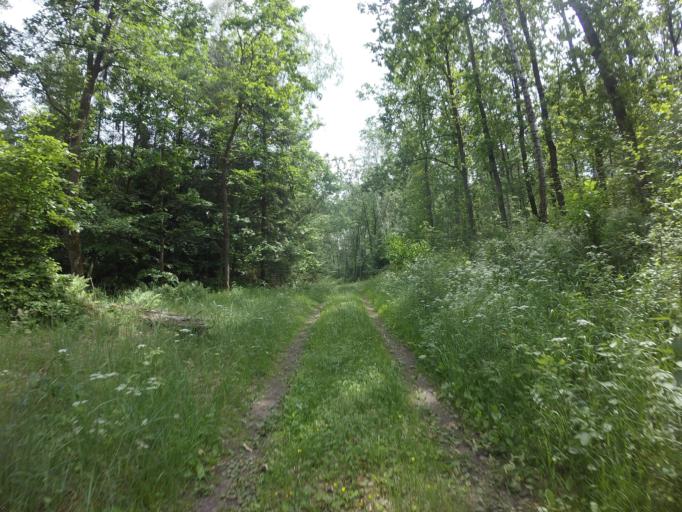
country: PL
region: West Pomeranian Voivodeship
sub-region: Powiat stargardzki
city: Dobrzany
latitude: 53.3332
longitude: 15.4569
